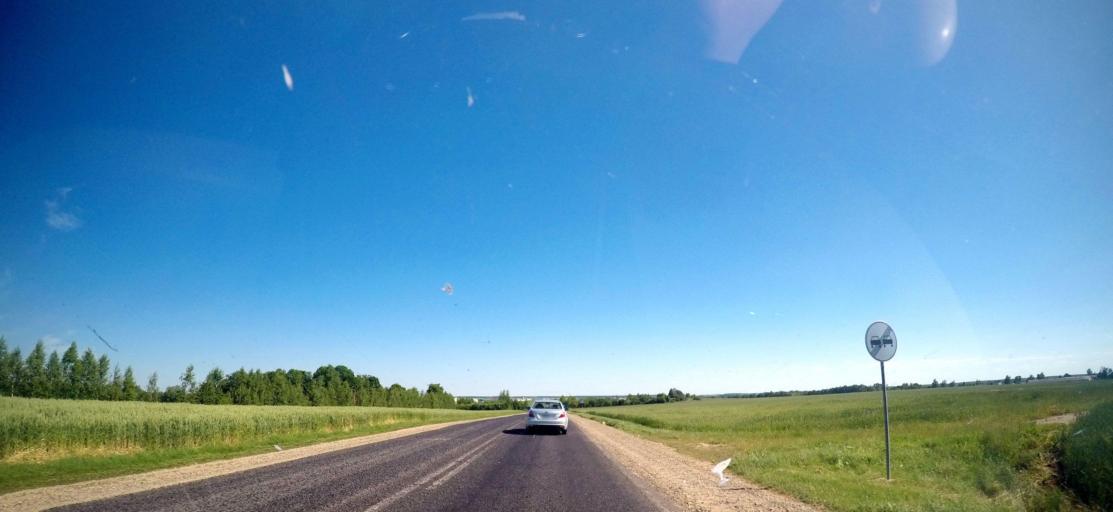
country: BY
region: Grodnenskaya
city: Vyalikaya Byerastavitsa
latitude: 53.2146
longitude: 24.0012
